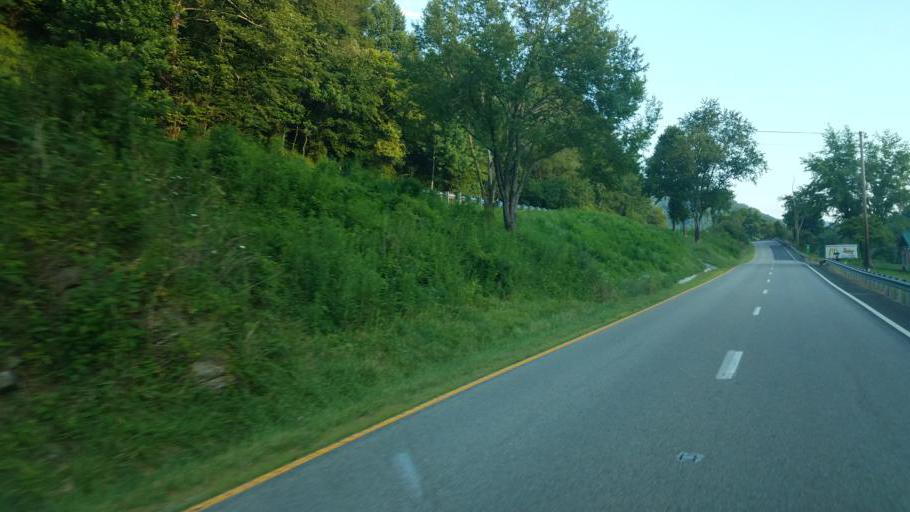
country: US
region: Virginia
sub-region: Wise County
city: Big Stone Gap
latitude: 36.7422
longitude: -82.7968
